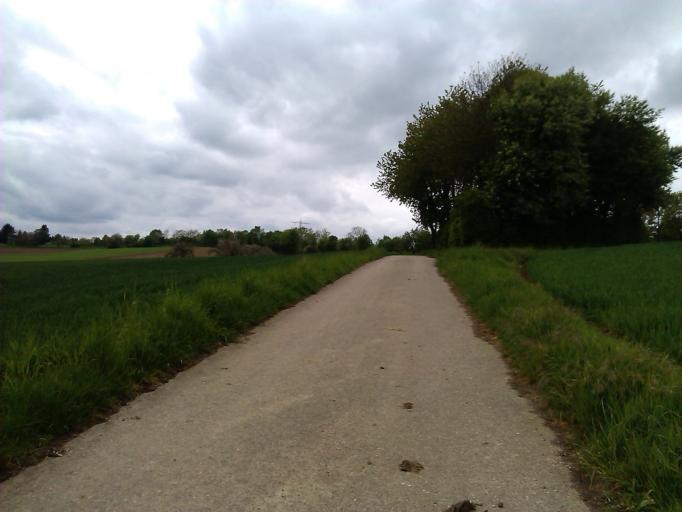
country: DE
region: Baden-Wuerttemberg
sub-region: Karlsruhe Region
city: Woessingen
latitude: 49.0212
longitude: 8.6163
